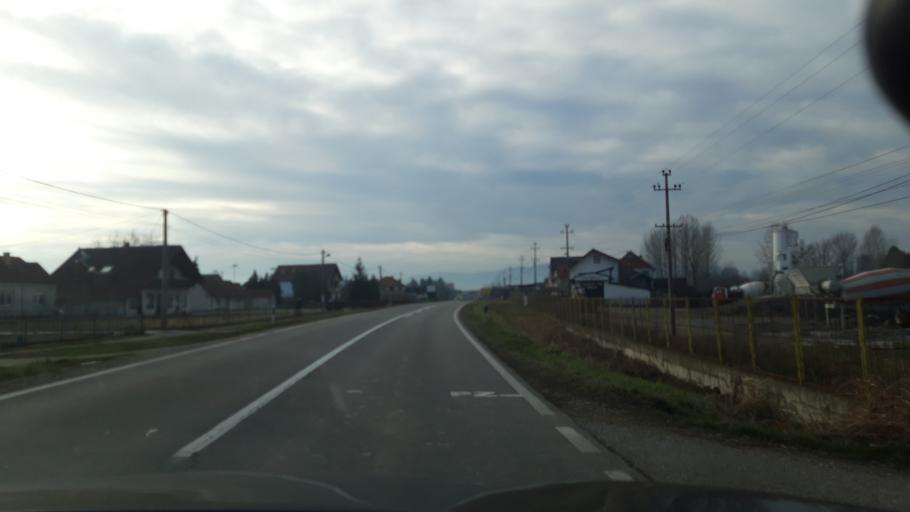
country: RS
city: Lipnicki Sor
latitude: 44.5877
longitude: 19.2576
